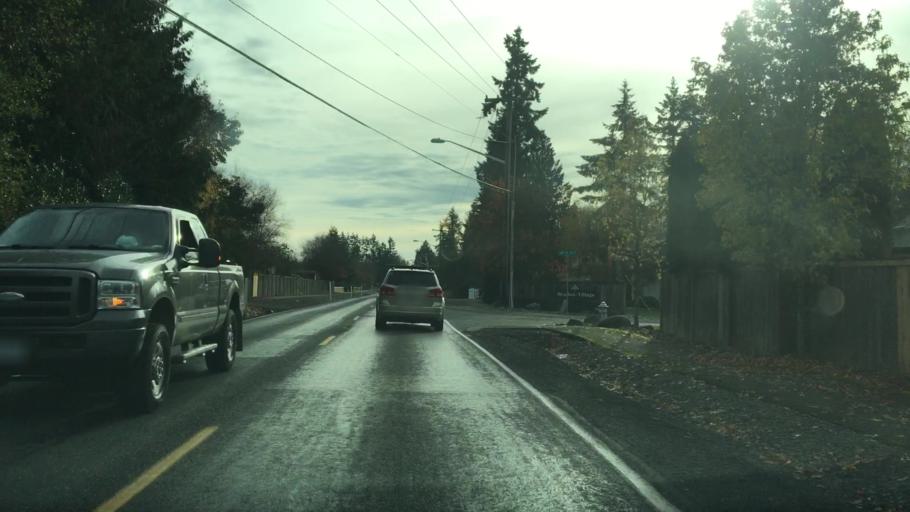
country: US
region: Washington
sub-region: Pierce County
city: South Hill
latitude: 47.1220
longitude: -122.3149
